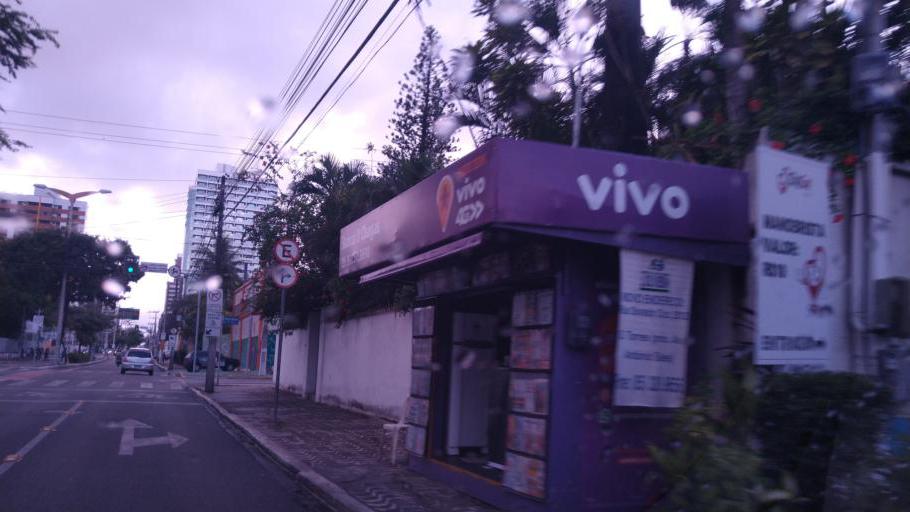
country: BR
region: Ceara
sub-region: Fortaleza
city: Fortaleza
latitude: -3.7365
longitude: -38.4931
